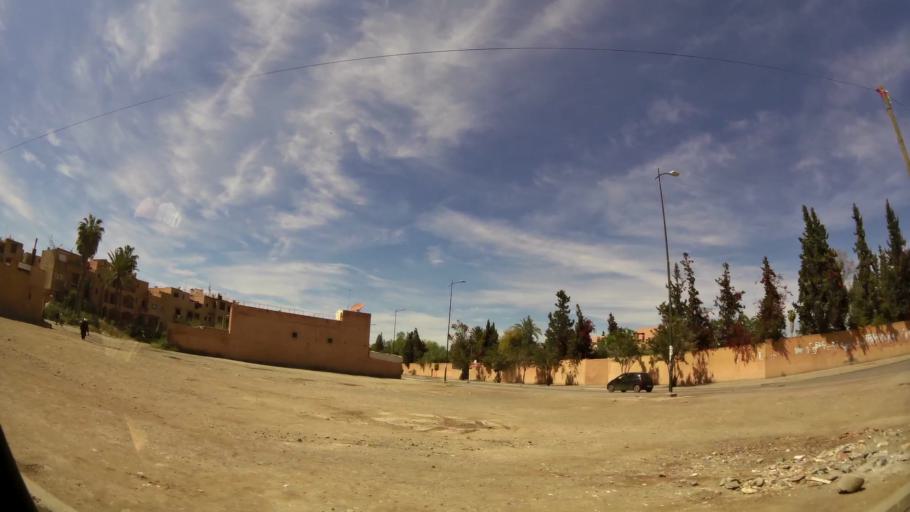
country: MA
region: Marrakech-Tensift-Al Haouz
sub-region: Marrakech
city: Marrakesh
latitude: 31.6625
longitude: -7.9992
